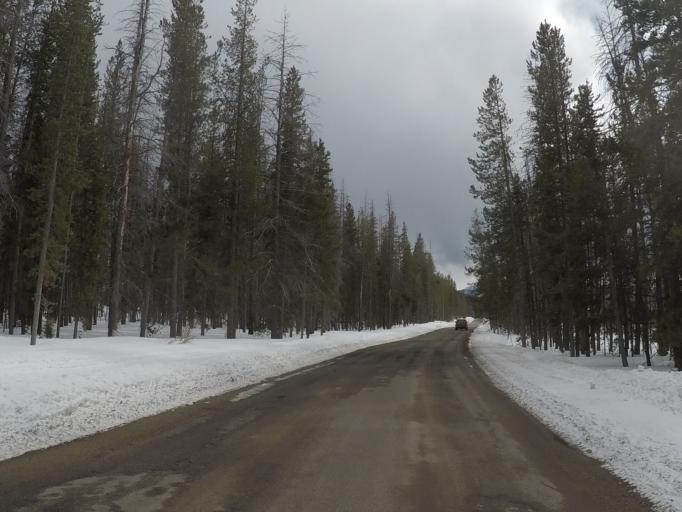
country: US
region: Montana
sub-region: Granite County
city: Philipsburg
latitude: 46.2074
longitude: -113.2508
